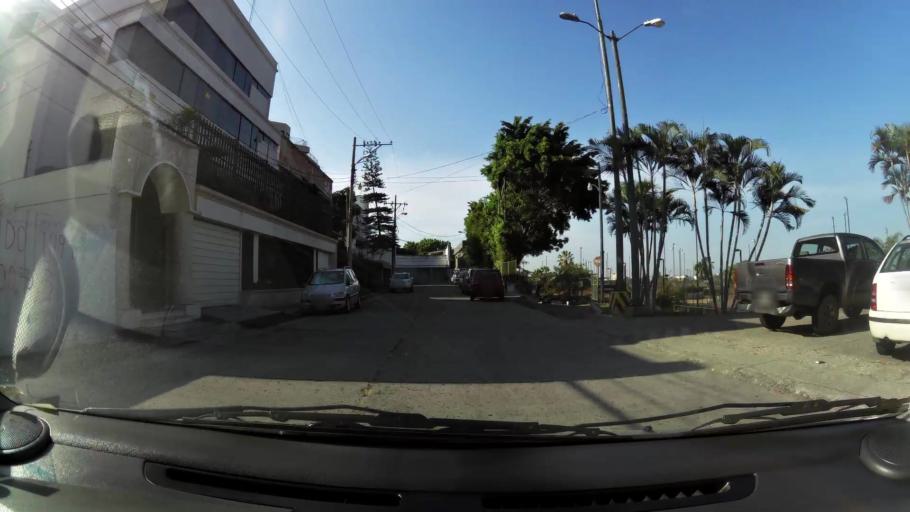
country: EC
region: Guayas
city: Guayaquil
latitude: -2.1638
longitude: -79.9058
